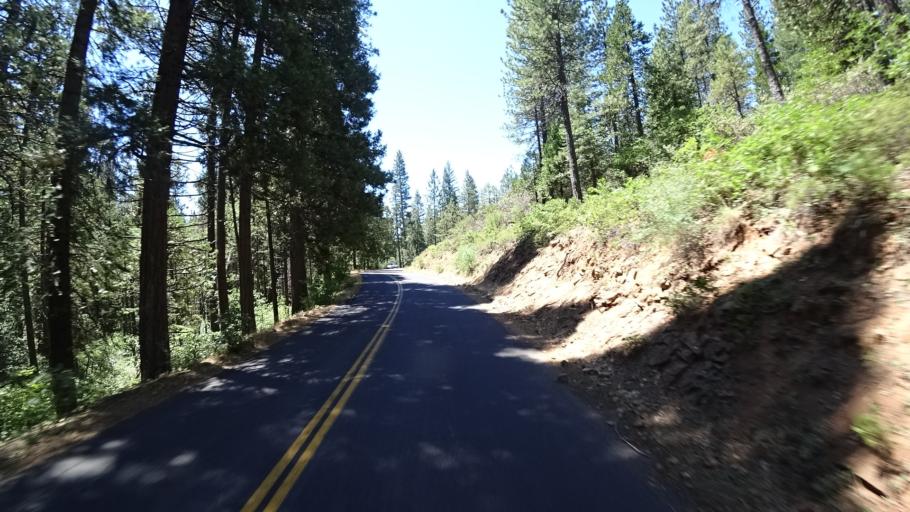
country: US
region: California
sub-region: Calaveras County
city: Arnold
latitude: 38.2281
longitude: -120.3565
